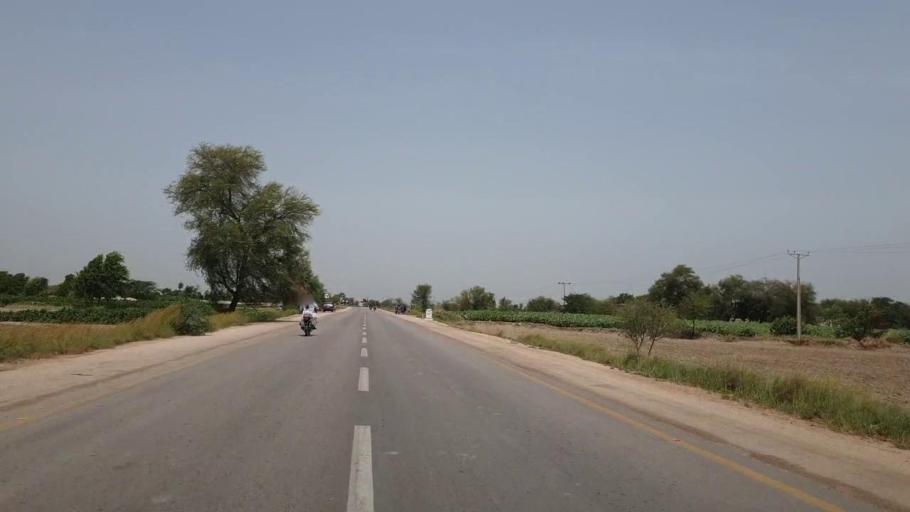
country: PK
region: Sindh
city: Shahpur Chakar
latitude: 26.1912
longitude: 68.5777
